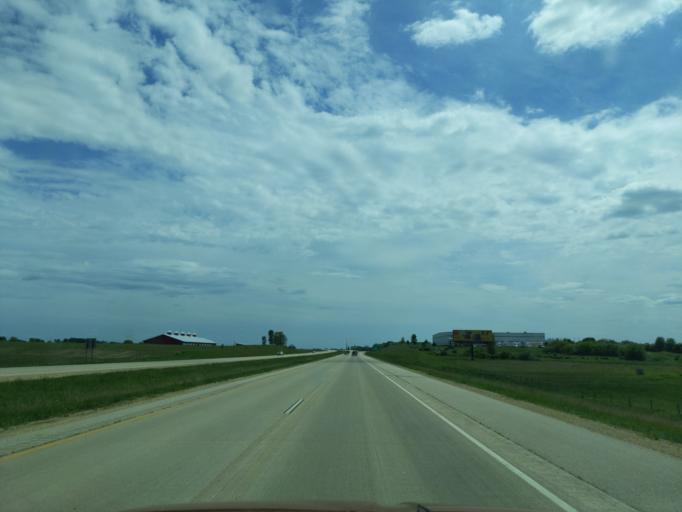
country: US
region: Wisconsin
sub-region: Dane County
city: De Forest
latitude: 43.2621
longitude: -89.3248
